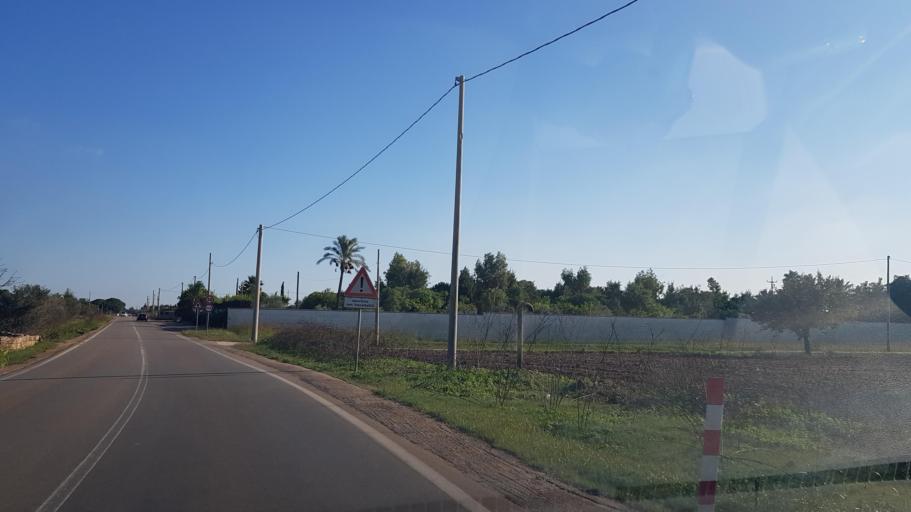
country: IT
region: Apulia
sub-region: Provincia di Lecce
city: Montesano Salentino
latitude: 39.9685
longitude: 18.3288
